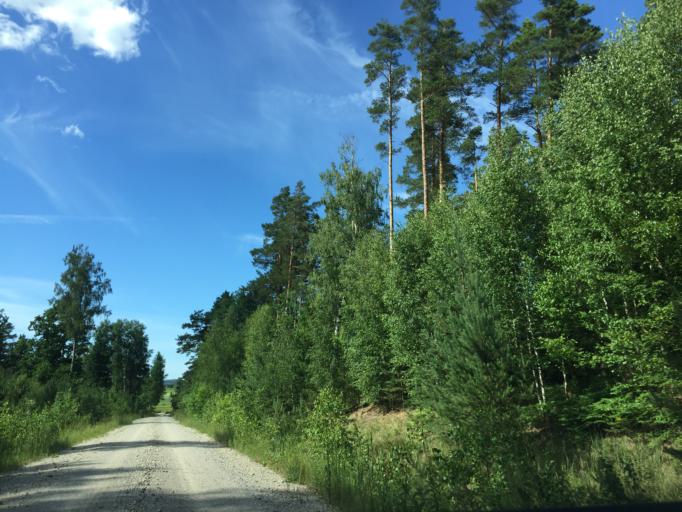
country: LV
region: Ventspils Rajons
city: Piltene
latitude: 57.1065
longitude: 21.8131
